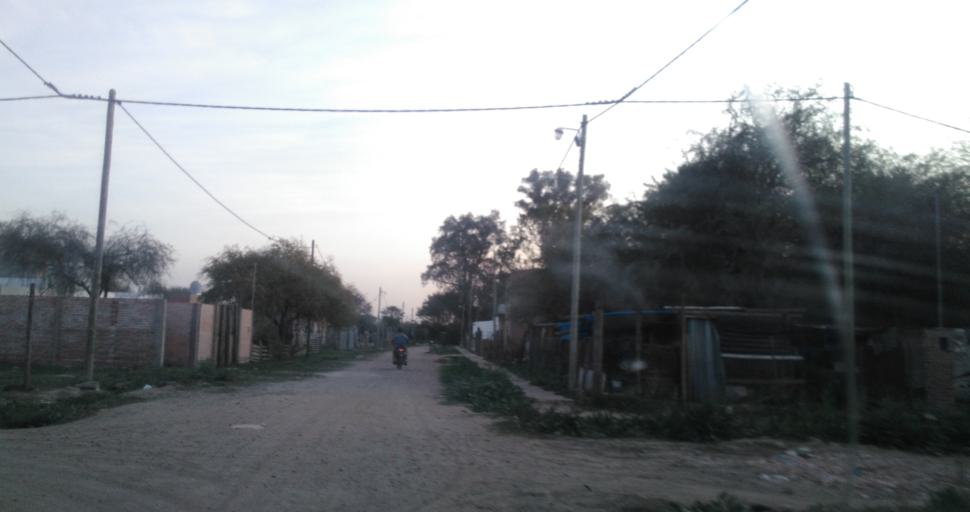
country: AR
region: Chaco
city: Resistencia
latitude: -27.4624
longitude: -59.0198
